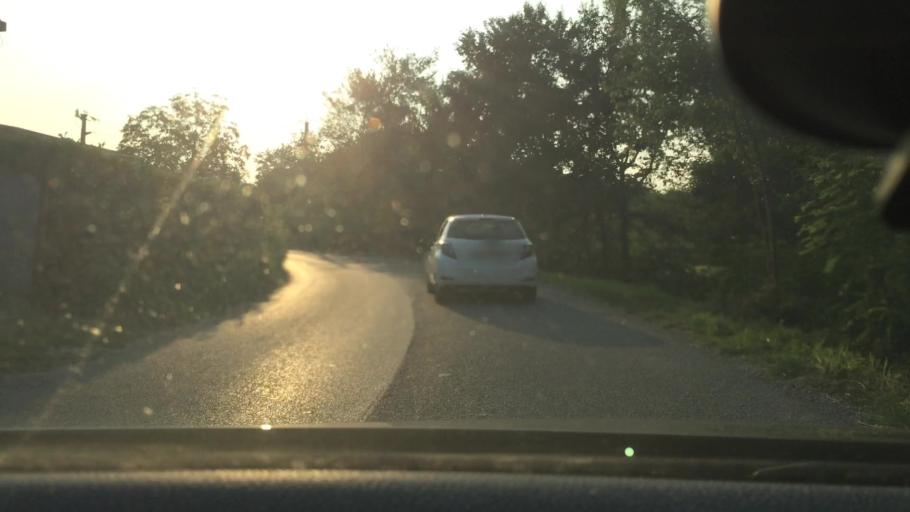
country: IT
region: Lombardy
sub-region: Provincia di Bergamo
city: Brembate di Sopra
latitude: 45.7137
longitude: 9.5672
